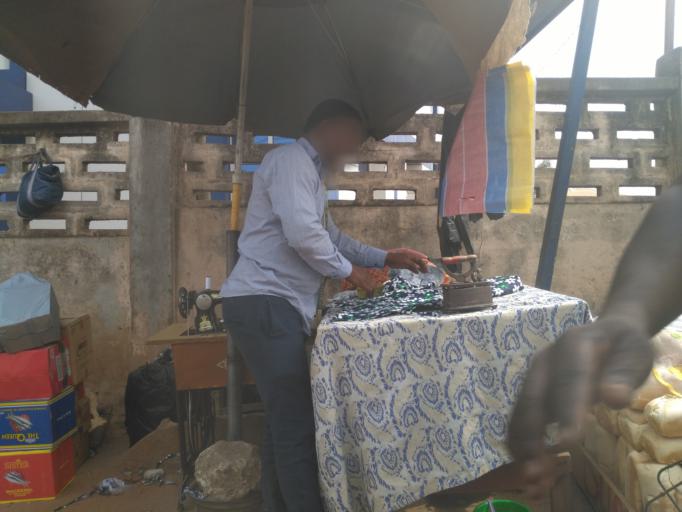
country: GH
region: Ashanti
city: Kumasi
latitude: 6.7021
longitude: -1.6224
